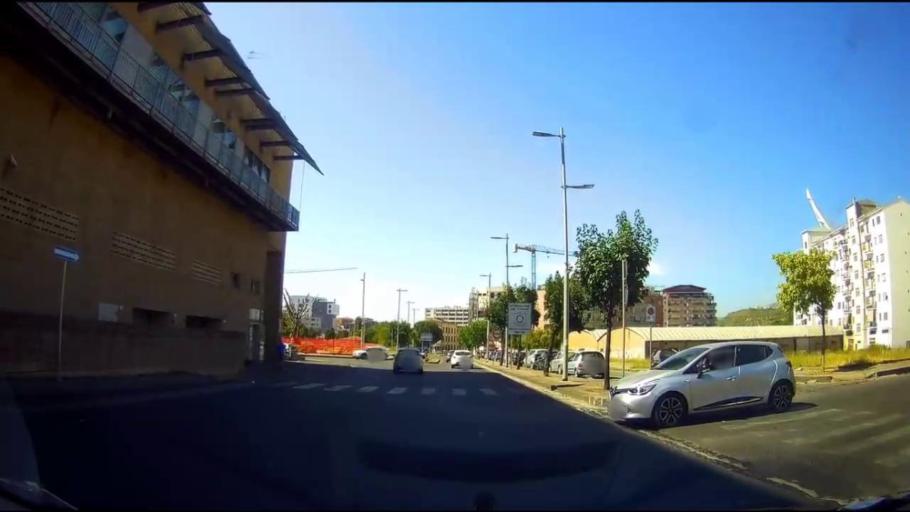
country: IT
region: Calabria
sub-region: Provincia di Cosenza
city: Cosenza
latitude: 39.2957
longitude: 16.2575
